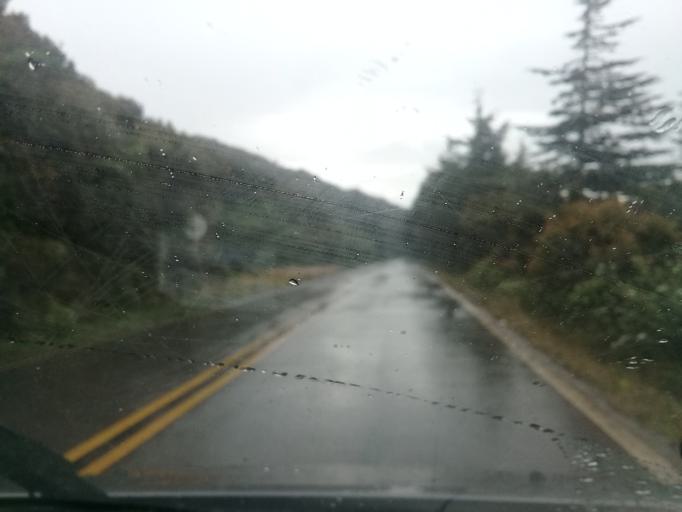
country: CO
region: Cundinamarca
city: Guasca
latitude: 4.8468
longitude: -73.8212
